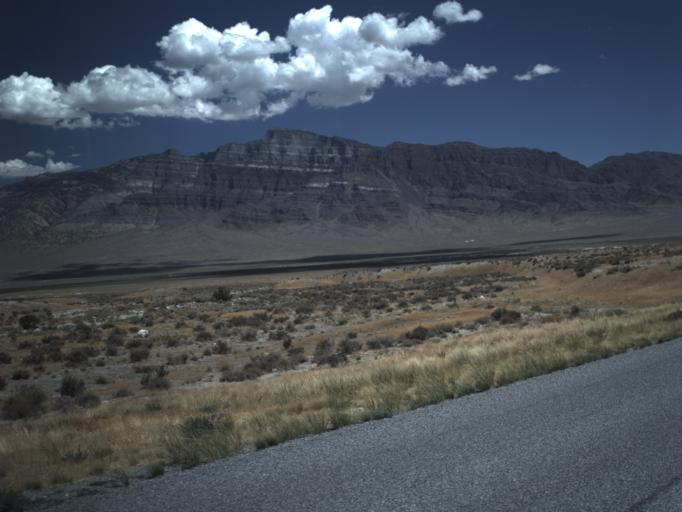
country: US
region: Utah
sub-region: Beaver County
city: Milford
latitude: 39.0852
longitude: -113.5178
